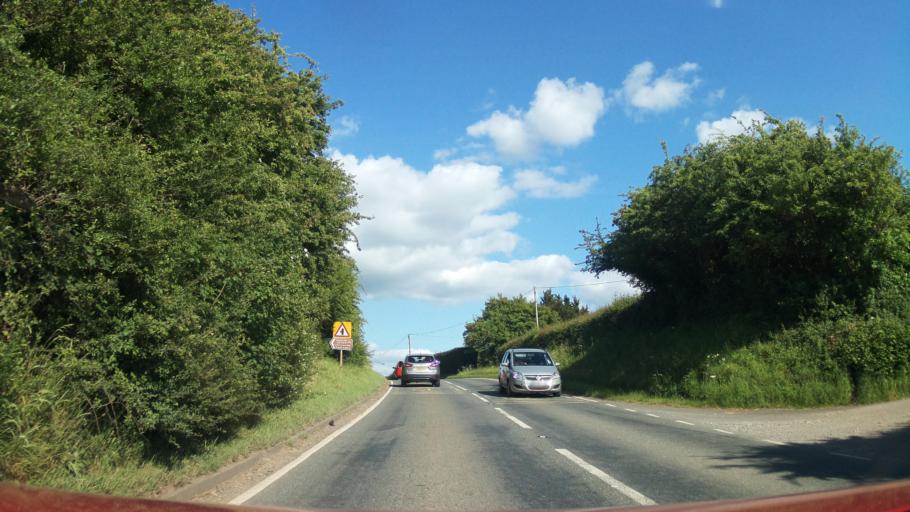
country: GB
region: England
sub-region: Somerset
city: North Petherton
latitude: 51.0480
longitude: -2.9918
